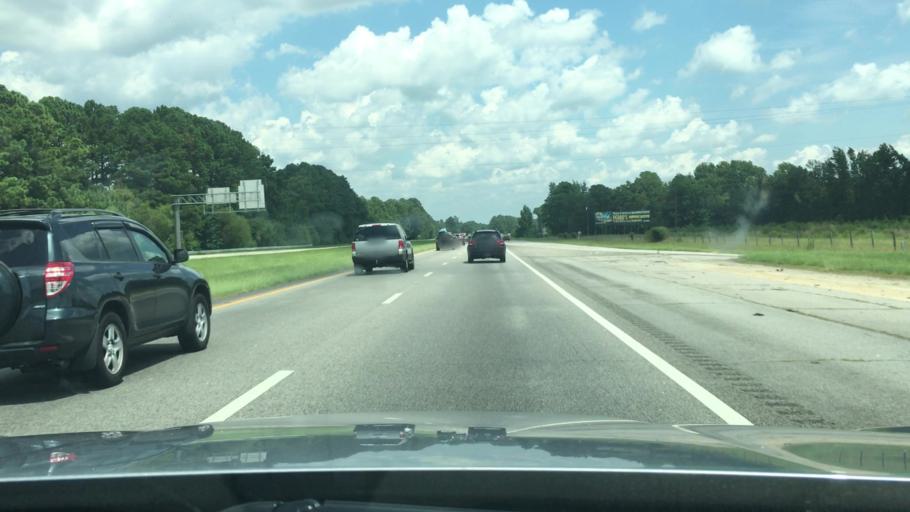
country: US
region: South Carolina
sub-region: Dillon County
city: Latta
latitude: 34.3442
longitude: -79.5317
